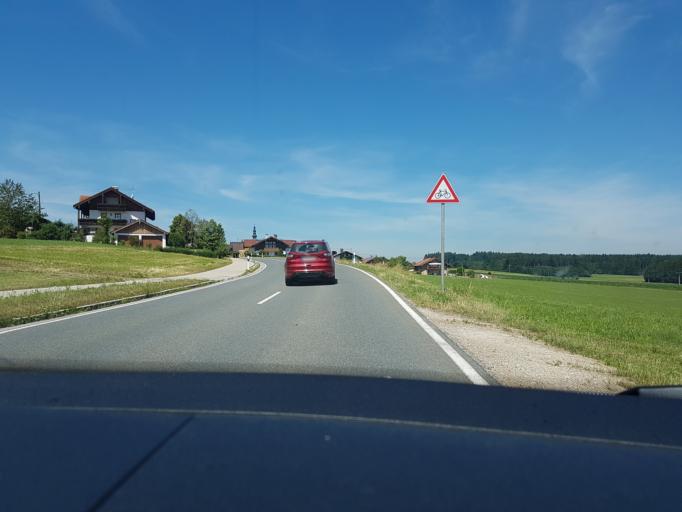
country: DE
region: Bavaria
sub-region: Upper Bavaria
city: Anger
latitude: 47.8373
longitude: 12.8992
